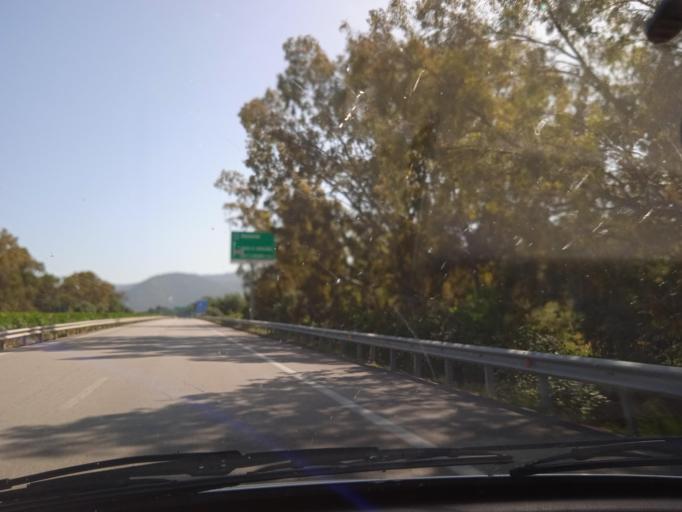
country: IT
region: Sicily
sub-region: Messina
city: Rocca di Capri Leone
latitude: 38.0970
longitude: 14.7058
